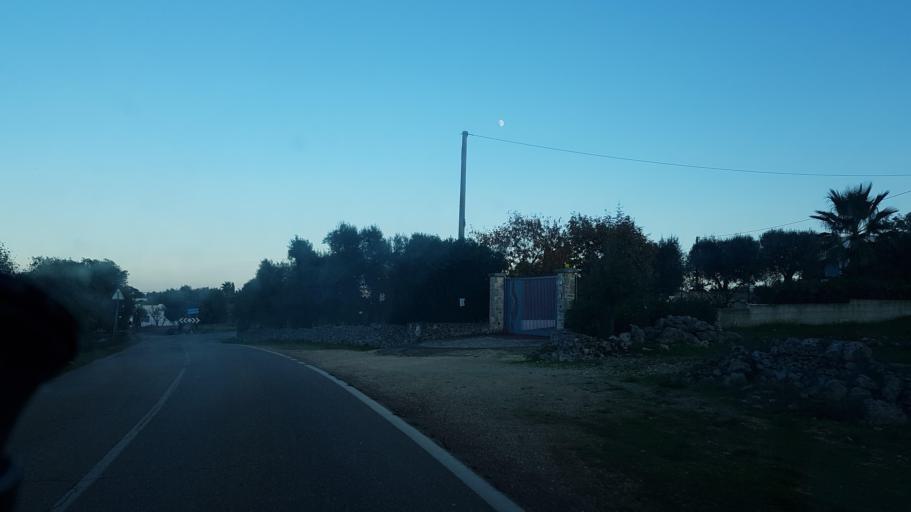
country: IT
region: Apulia
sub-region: Provincia di Brindisi
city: Ostuni
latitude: 40.6959
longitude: 17.5936
